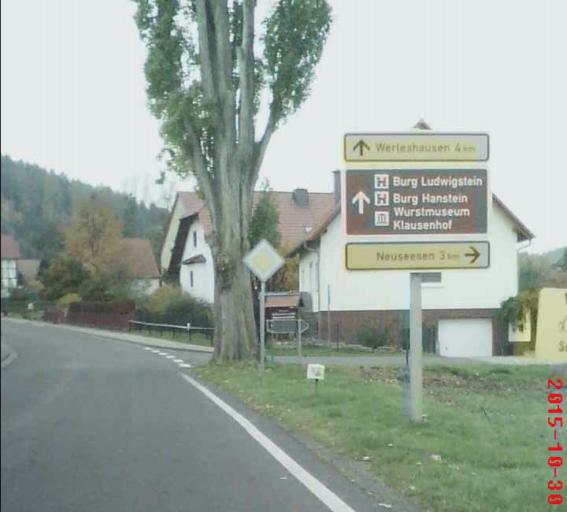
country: DE
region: Thuringia
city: Bornhagen
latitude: 51.3460
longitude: 9.9463
